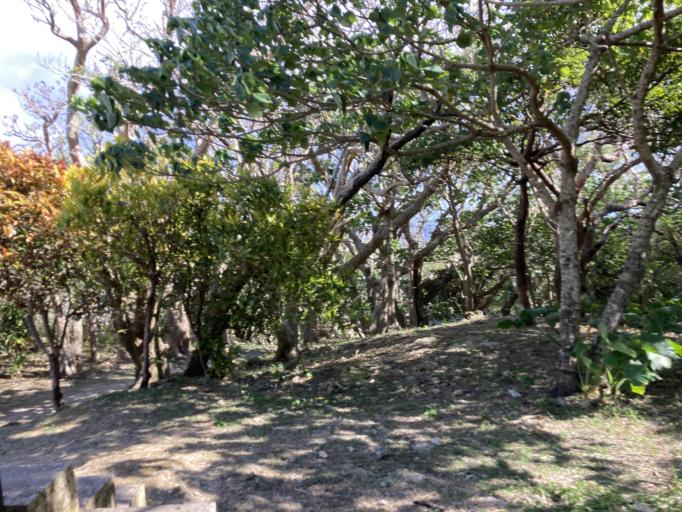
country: JP
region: Okinawa
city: Tomigusuku
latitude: 26.1441
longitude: 127.7810
